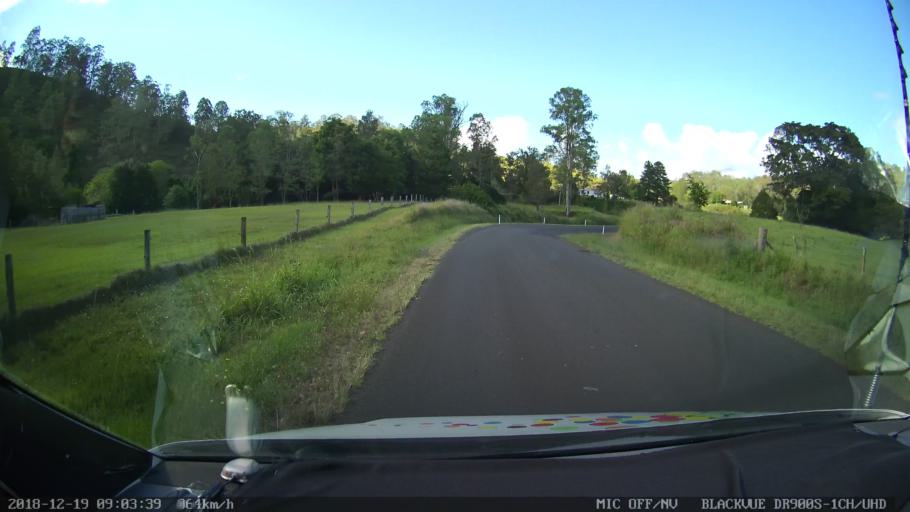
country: AU
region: New South Wales
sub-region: Kyogle
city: Kyogle
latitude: -28.4495
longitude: 152.9500
